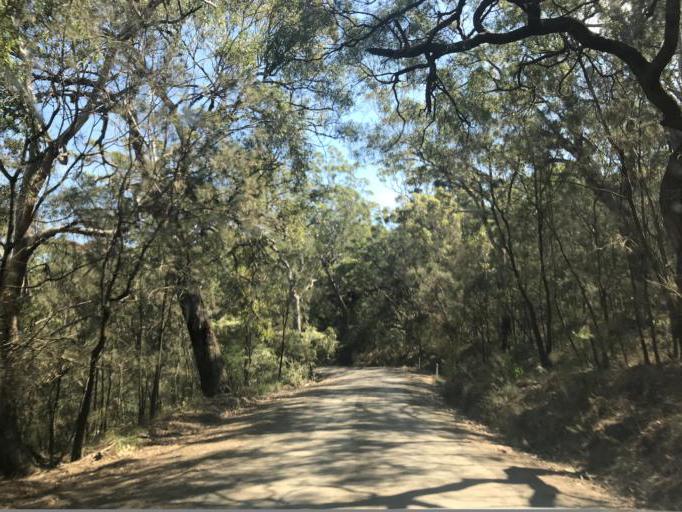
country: AU
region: New South Wales
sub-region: Hawkesbury
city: Pitt Town
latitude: -33.4081
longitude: 150.9260
